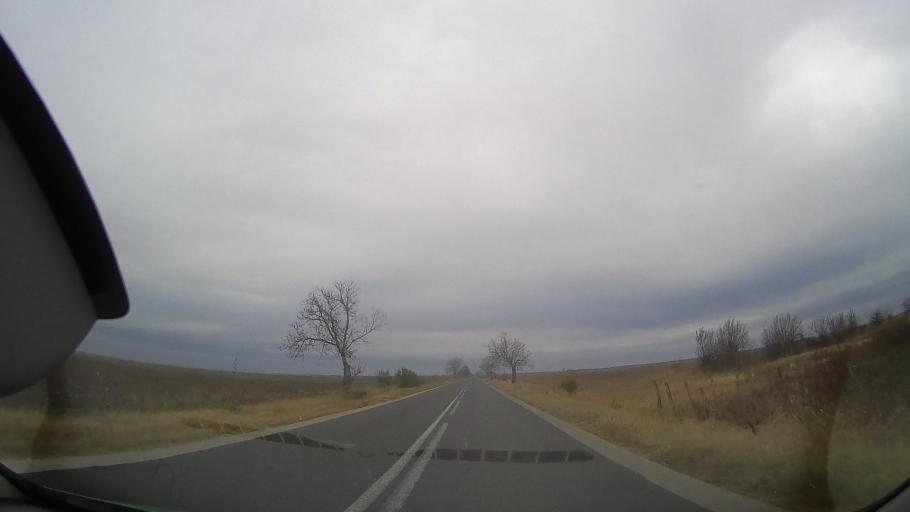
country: RO
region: Ialomita
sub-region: Comuna Milosesti
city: Milosesti
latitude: 44.7741
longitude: 27.1766
